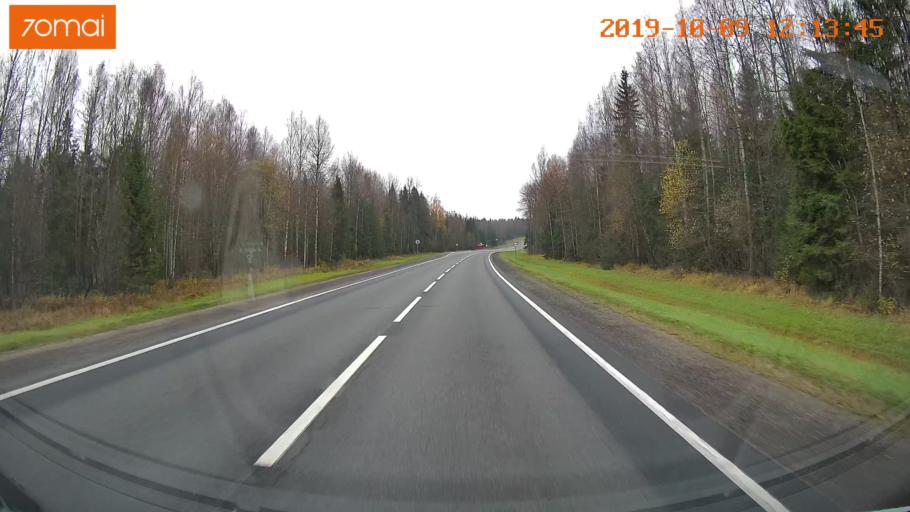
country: RU
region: Jaroslavl
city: Prechistoye
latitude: 58.5056
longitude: 40.3440
